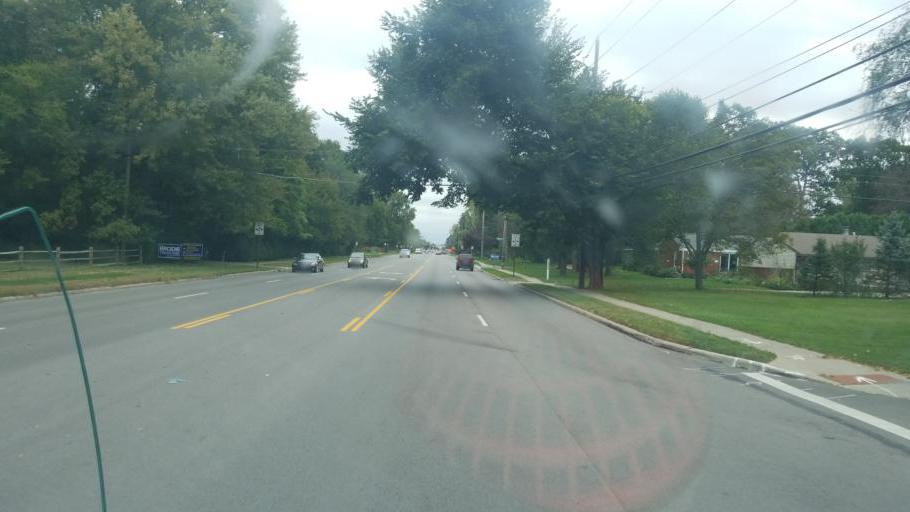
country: US
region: Ohio
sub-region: Lucas County
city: Ottawa Hills
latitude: 41.6771
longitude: -83.6365
